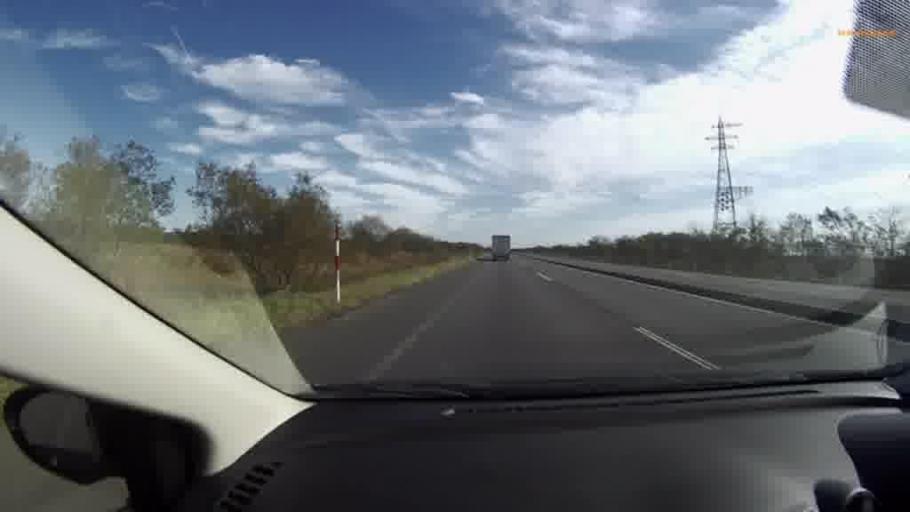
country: JP
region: Hokkaido
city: Kushiro
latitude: 43.0285
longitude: 144.2955
